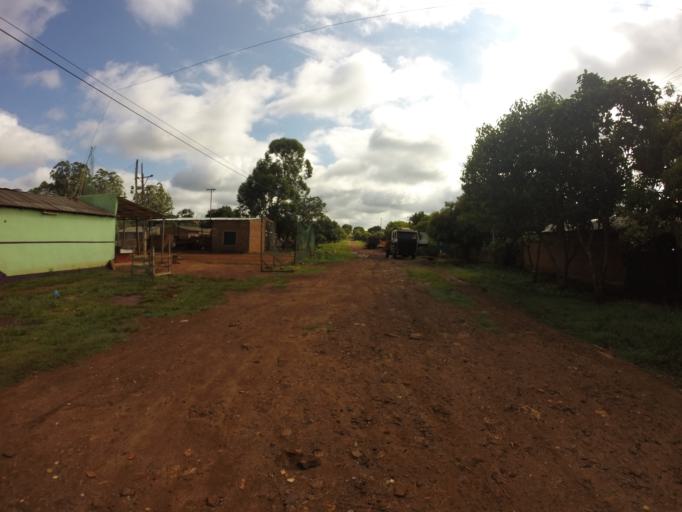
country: PY
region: Alto Parana
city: Ciudad del Este
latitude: -25.3949
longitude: -54.6464
